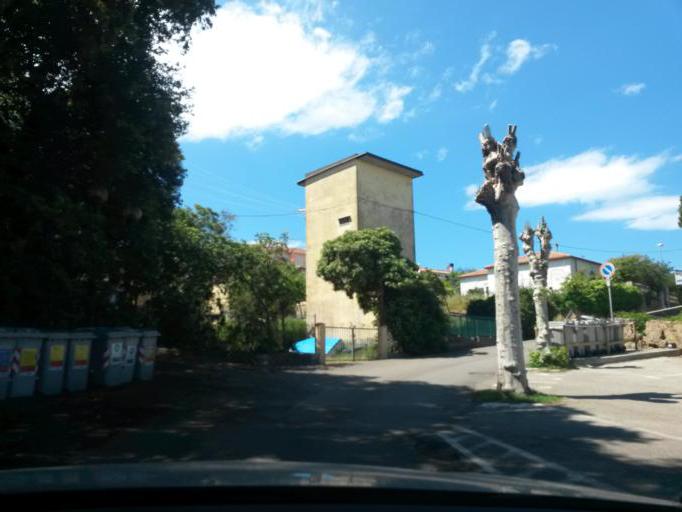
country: IT
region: Tuscany
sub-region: Provincia di Livorno
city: Rio Marina
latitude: 42.8641
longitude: 10.4200
